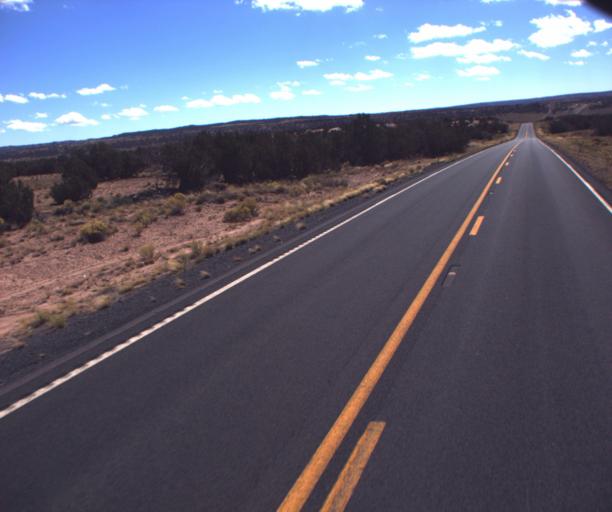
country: US
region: Arizona
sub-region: Apache County
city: Houck
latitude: 35.1072
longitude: -109.3167
